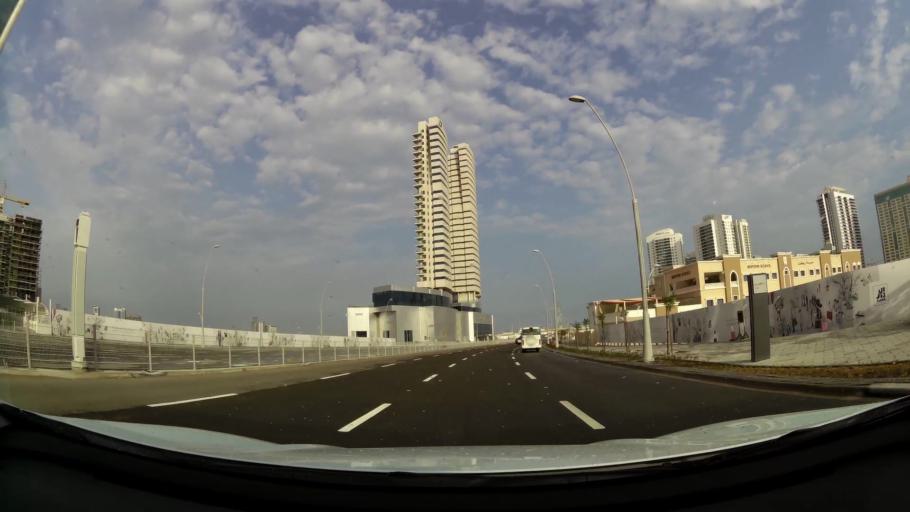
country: AE
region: Abu Dhabi
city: Abu Dhabi
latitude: 24.5064
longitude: 54.4071
